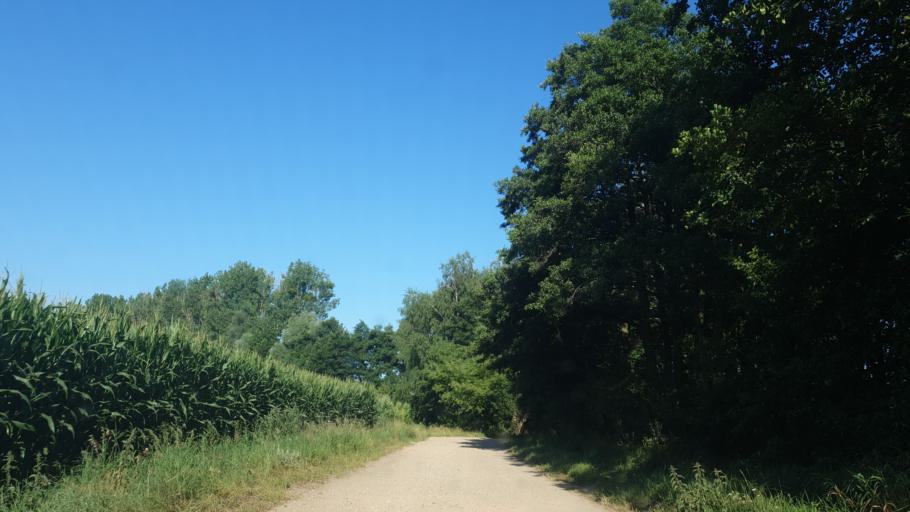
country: DE
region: Mecklenburg-Vorpommern
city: Ferdinandshof
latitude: 53.6535
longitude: 13.9499
